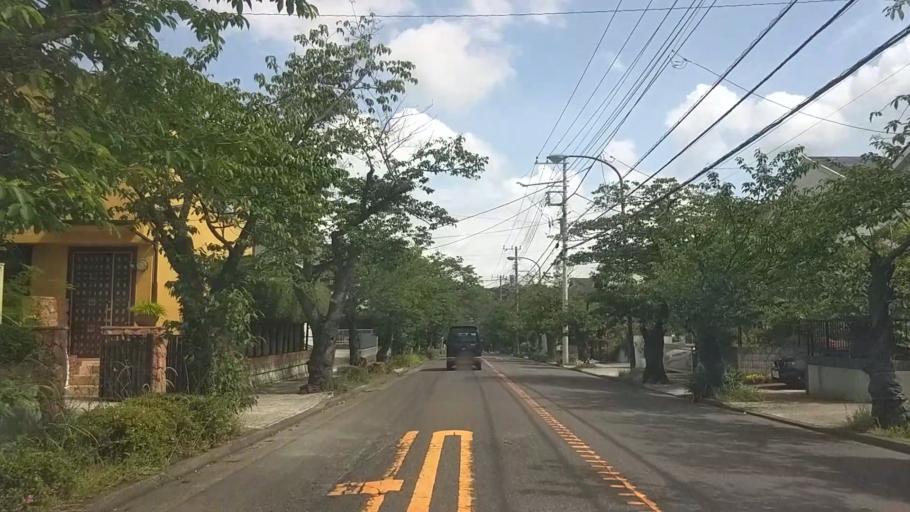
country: JP
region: Kanagawa
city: Zushi
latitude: 35.3141
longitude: 139.5768
